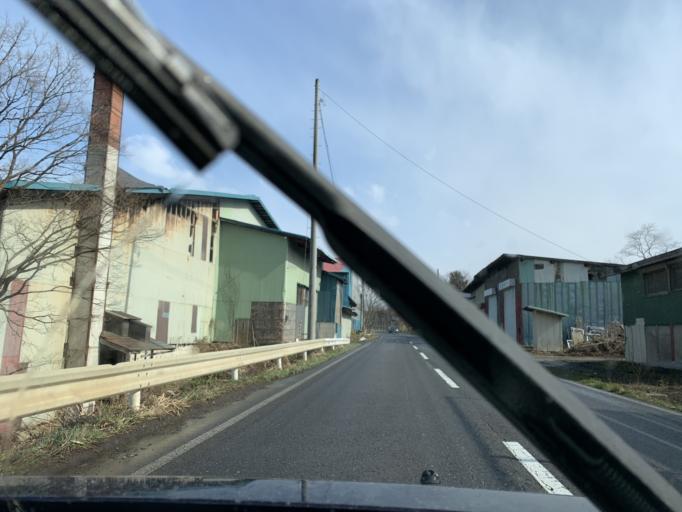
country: JP
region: Iwate
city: Kitakami
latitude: 39.2597
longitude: 141.0521
